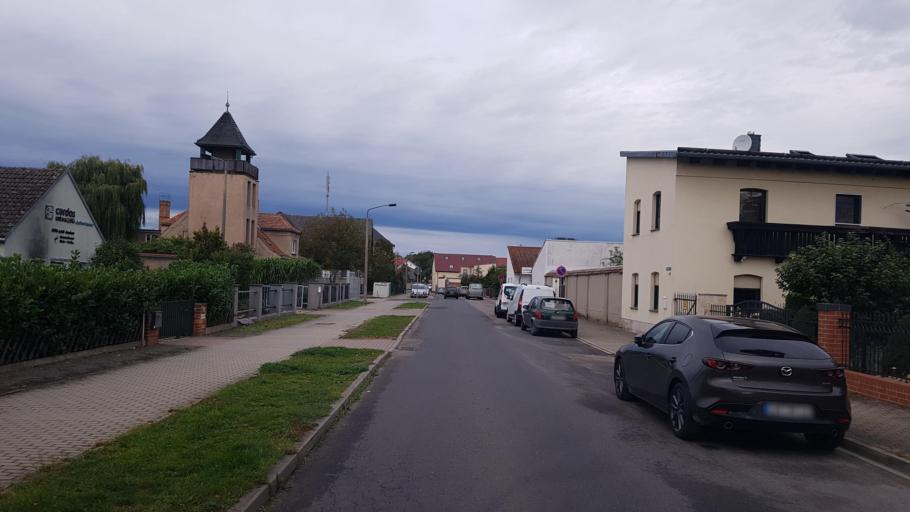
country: DE
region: Brandenburg
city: Golssen
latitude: 51.9695
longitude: 13.6047
